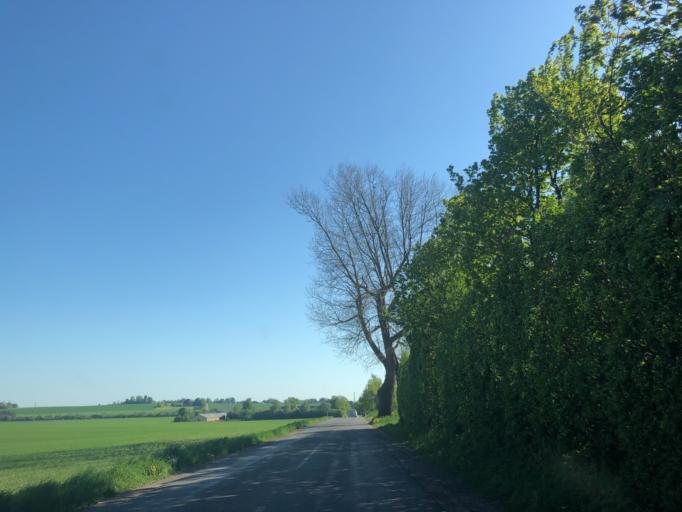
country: DK
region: Zealand
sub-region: Ringsted Kommune
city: Ringsted
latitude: 55.4460
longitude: 11.7294
